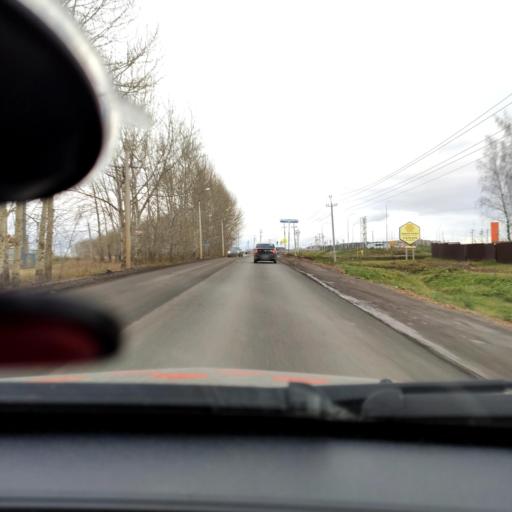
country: RU
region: Bashkortostan
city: Kabakovo
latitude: 54.6181
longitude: 56.1226
